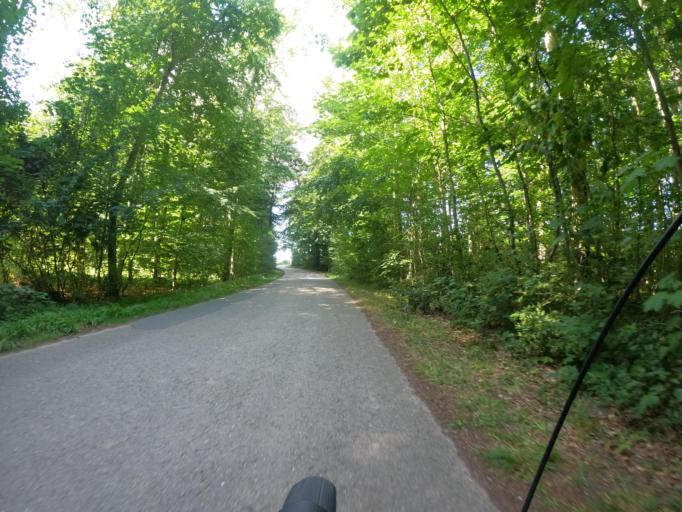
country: DE
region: Schleswig-Holstein
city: Dollerup
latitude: 54.7989
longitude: 9.7115
